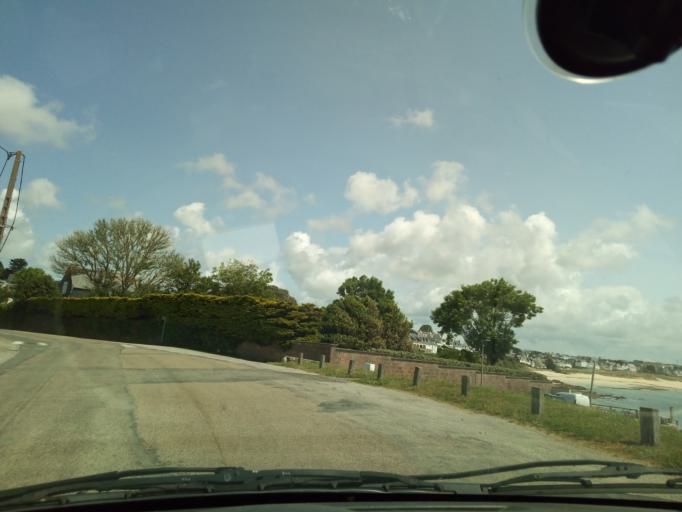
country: FR
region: Brittany
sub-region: Departement du Finistere
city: Esquibien
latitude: 48.0084
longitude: -4.5566
